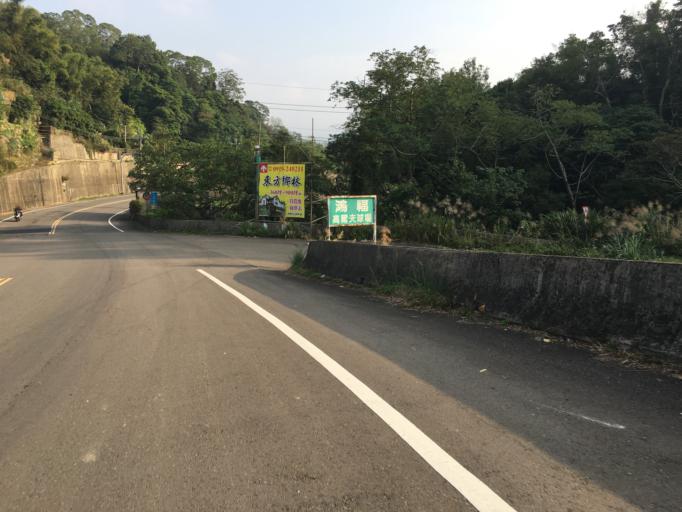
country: TW
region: Taiwan
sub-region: Hsinchu
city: Hsinchu
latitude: 24.7140
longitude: 121.0419
